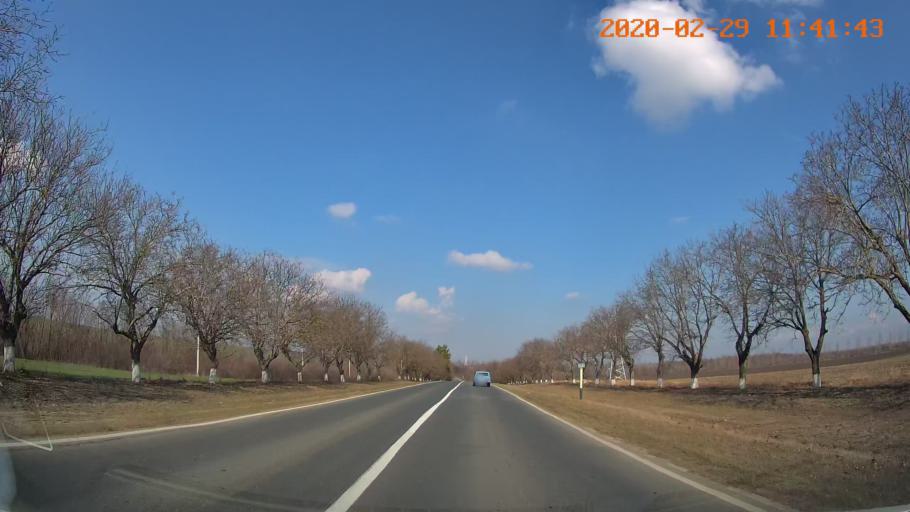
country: MD
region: Rezina
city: Saharna
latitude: 47.6756
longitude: 29.0154
